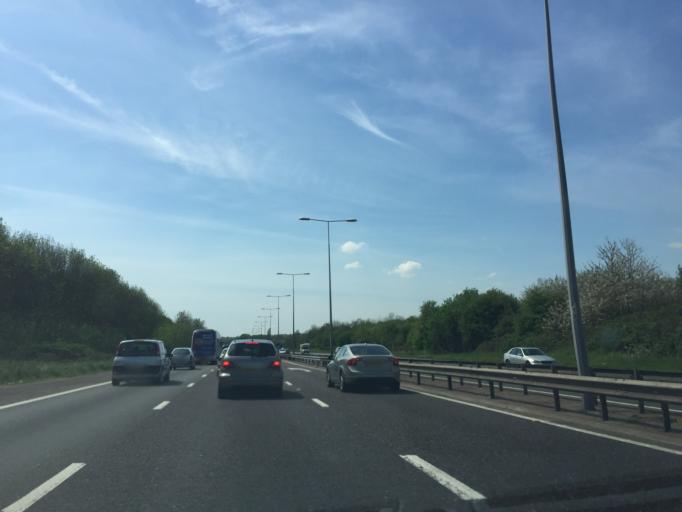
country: GB
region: England
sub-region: Essex
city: Chigwell
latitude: 51.6139
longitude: 0.0567
